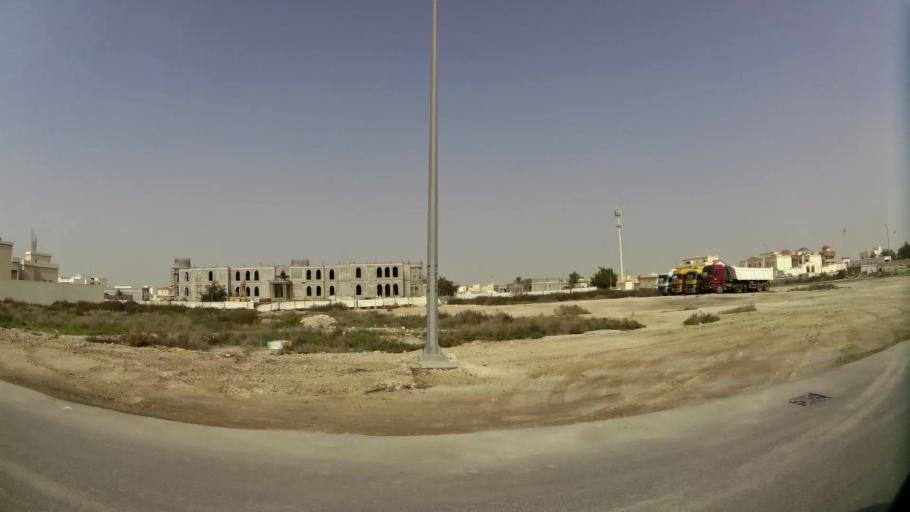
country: QA
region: Baladiyat ar Rayyan
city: Ar Rayyan
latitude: 25.2426
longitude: 51.4400
